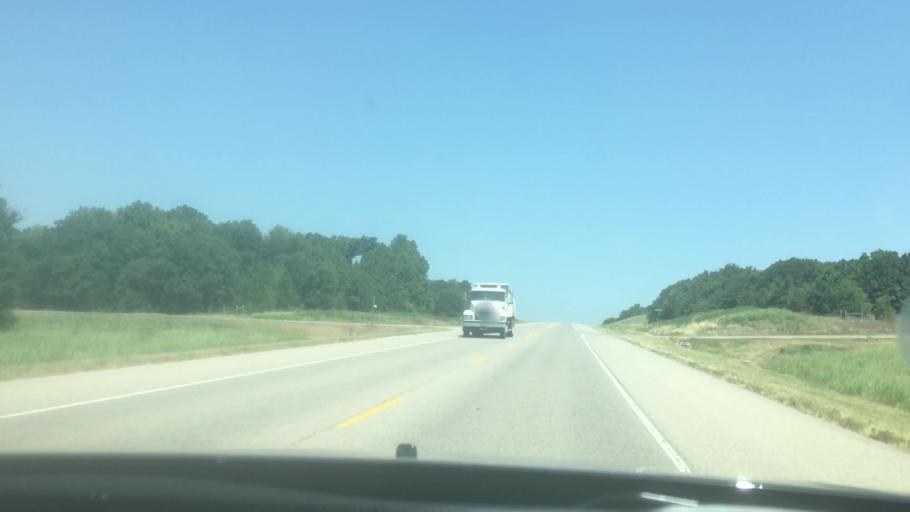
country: US
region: Oklahoma
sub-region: Pontotoc County
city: Ada
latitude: 34.6649
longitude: -96.5647
